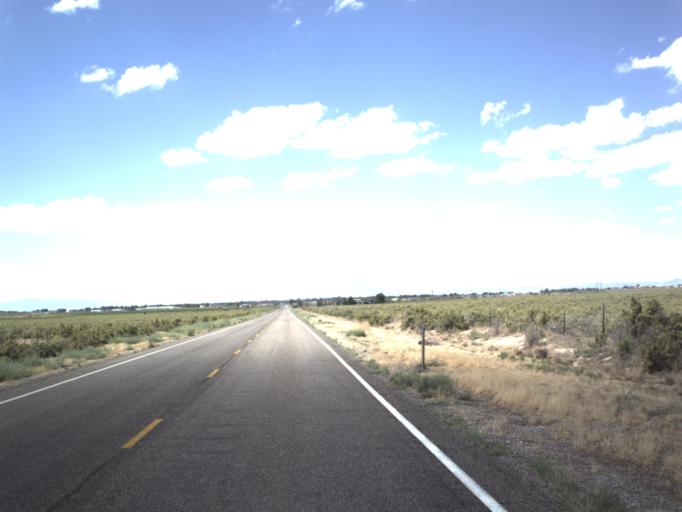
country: US
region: Utah
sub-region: Millard County
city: Delta
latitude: 39.3532
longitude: -112.5139
